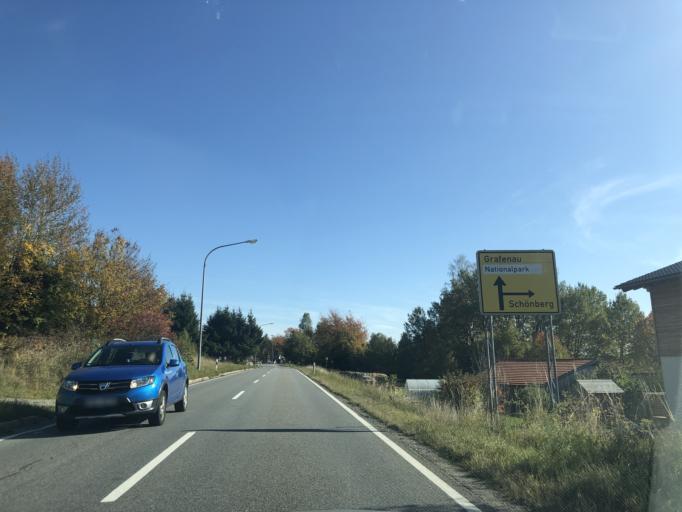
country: DE
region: Bavaria
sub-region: Lower Bavaria
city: Spiegelau
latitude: 48.9119
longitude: 13.3362
